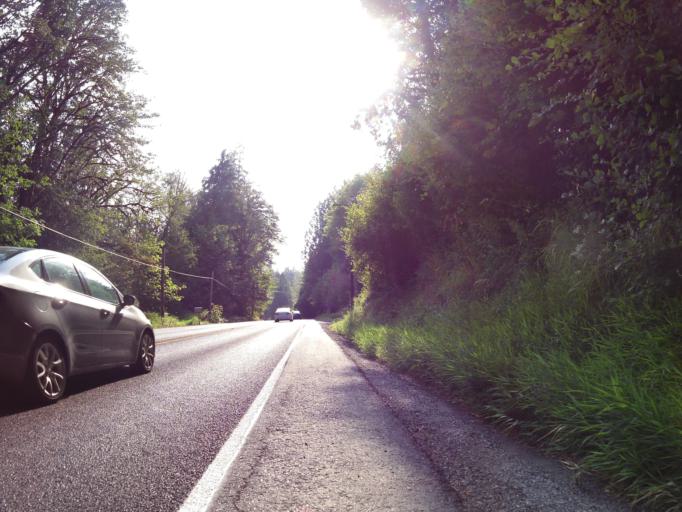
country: US
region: Washington
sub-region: Mason County
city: Belfair
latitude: 47.5028
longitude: -122.7988
